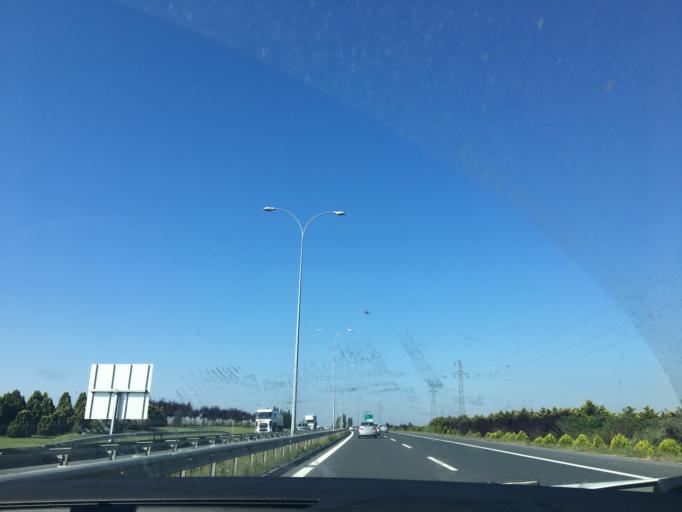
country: TR
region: Istanbul
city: Canta
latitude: 41.1089
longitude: 28.1625
